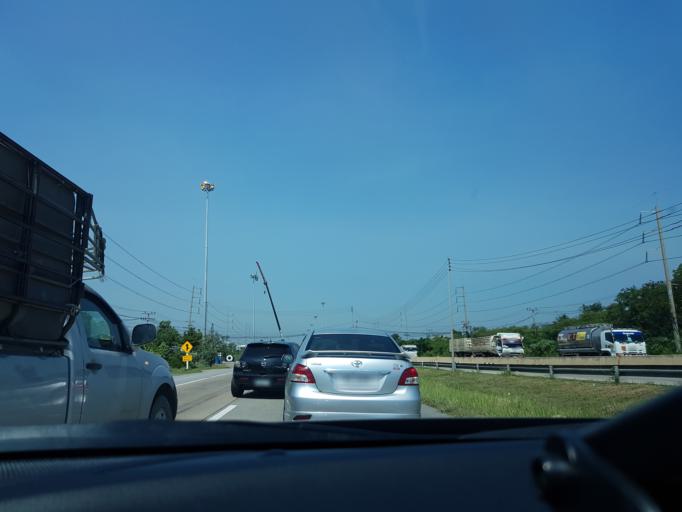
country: TH
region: Sara Buri
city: Saraburi
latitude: 14.5025
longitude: 100.9152
